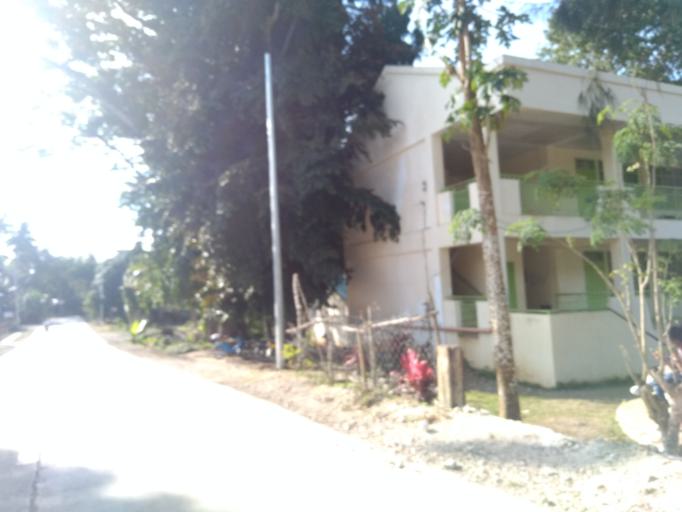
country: PH
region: Central Visayas
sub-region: Province of Siquijor
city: Siquijor
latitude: 9.1817
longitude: 123.5406
